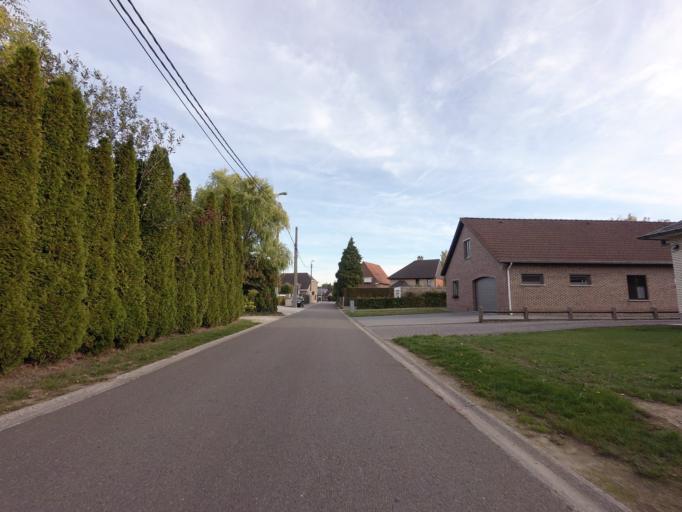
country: BE
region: Flanders
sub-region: Provincie Vlaams-Brabant
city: Kortenberg
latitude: 50.8937
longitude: 4.5841
